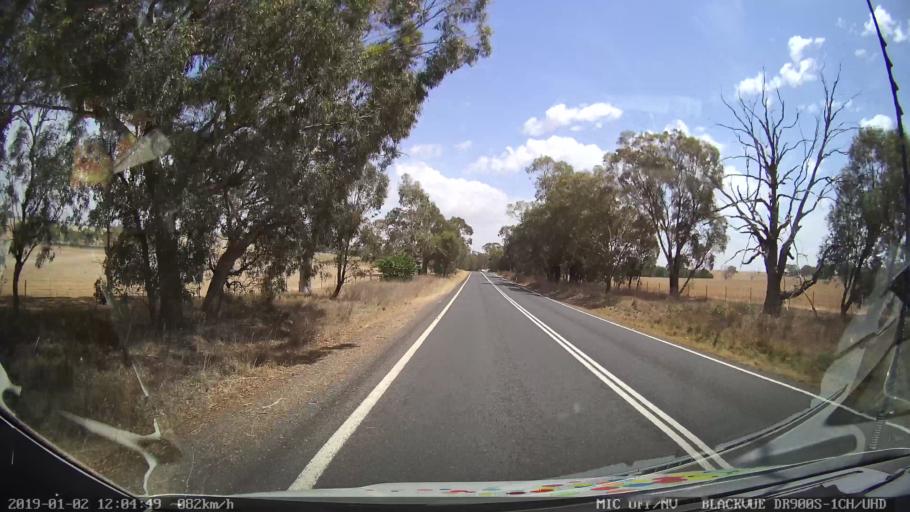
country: AU
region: New South Wales
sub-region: Young
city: Young
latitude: -34.5212
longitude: 148.3066
